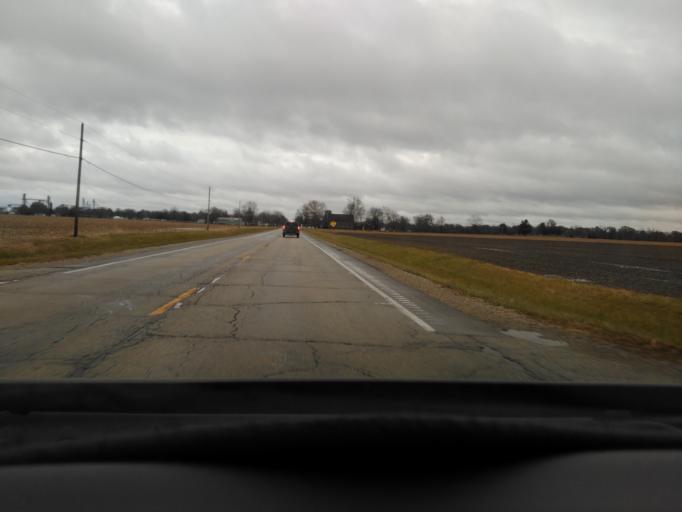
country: US
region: Illinois
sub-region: Effingham County
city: Altamont
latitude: 39.0493
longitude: -88.7669
